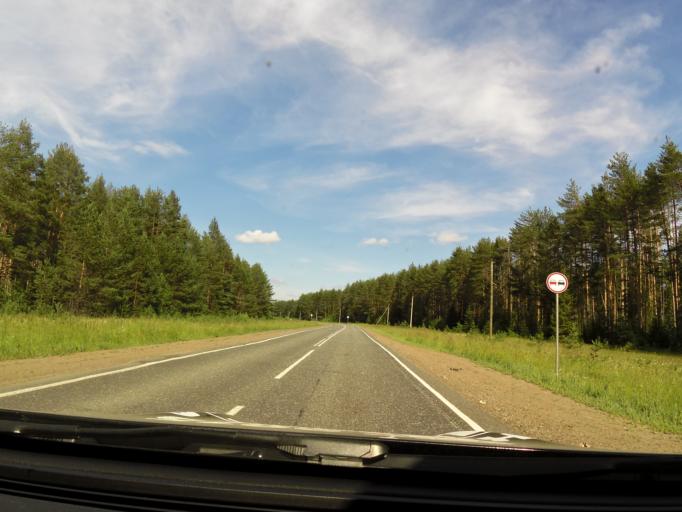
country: RU
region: Kirov
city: Belaya Kholunitsa
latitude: 58.8422
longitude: 50.8011
